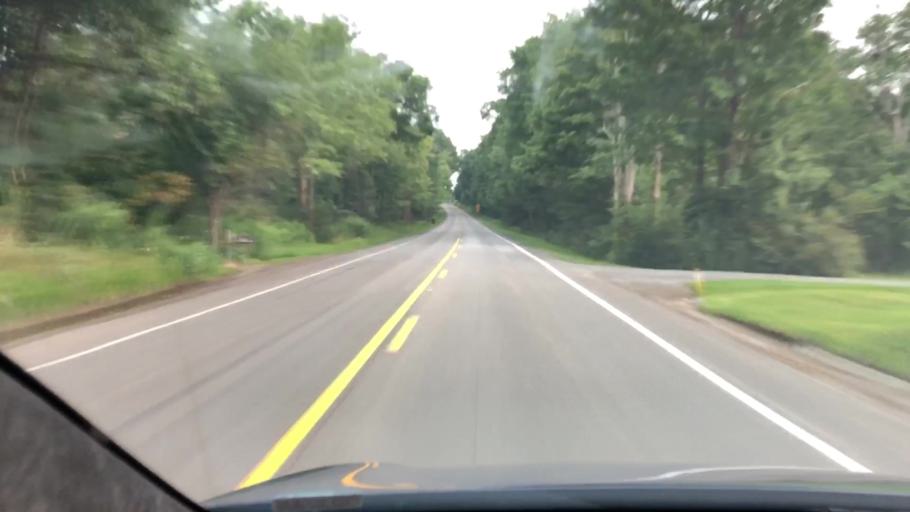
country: US
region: Pennsylvania
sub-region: Butler County
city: Slippery Rock
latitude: 41.0801
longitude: -80.0024
